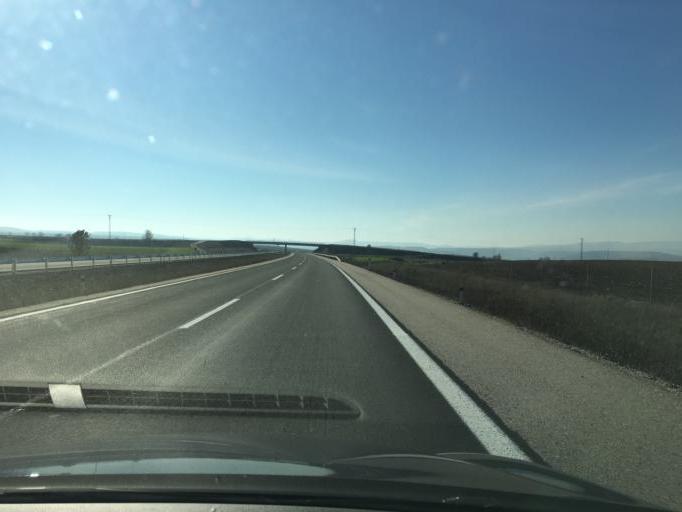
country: ES
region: Castille and Leon
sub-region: Provincia de Burgos
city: Briviesca
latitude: 42.5534
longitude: -3.2830
